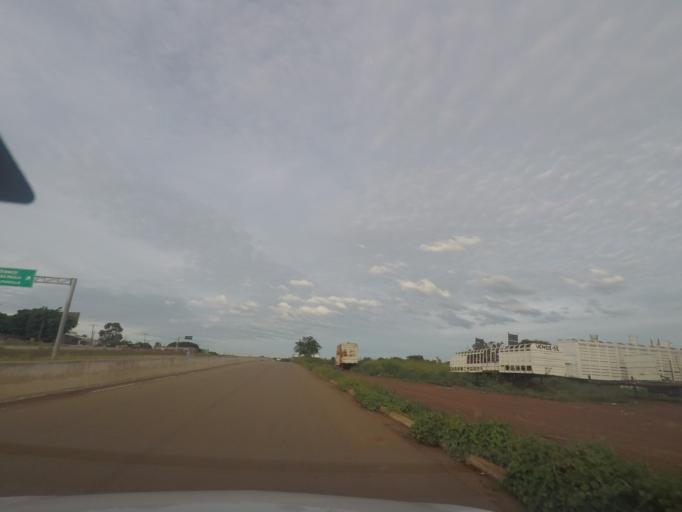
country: BR
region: Goias
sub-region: Goiania
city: Goiania
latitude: -16.7226
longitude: -49.3755
